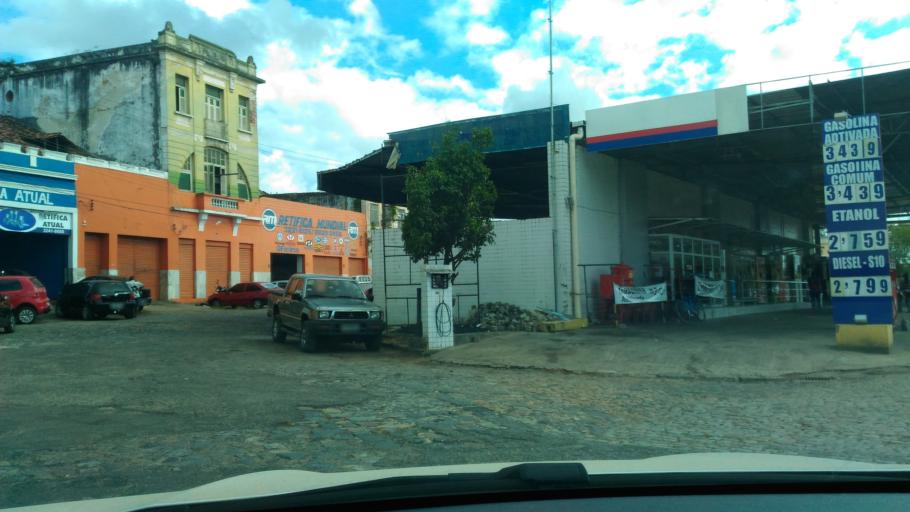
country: BR
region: Paraiba
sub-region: Joao Pessoa
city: Joao Pessoa
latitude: -7.1137
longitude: -34.8898
